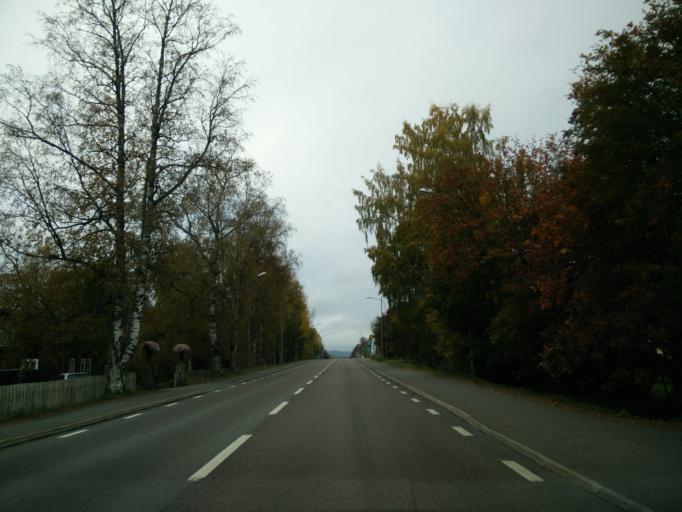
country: SE
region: Vaesternorrland
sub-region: Ange Kommun
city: Ange
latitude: 62.5189
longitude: 15.6525
